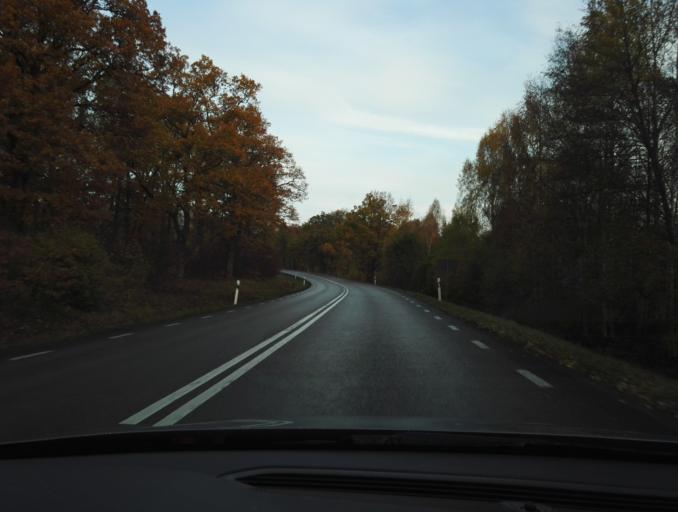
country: SE
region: Kronoberg
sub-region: Alvesta Kommun
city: Moheda
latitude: 56.9868
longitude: 14.6934
